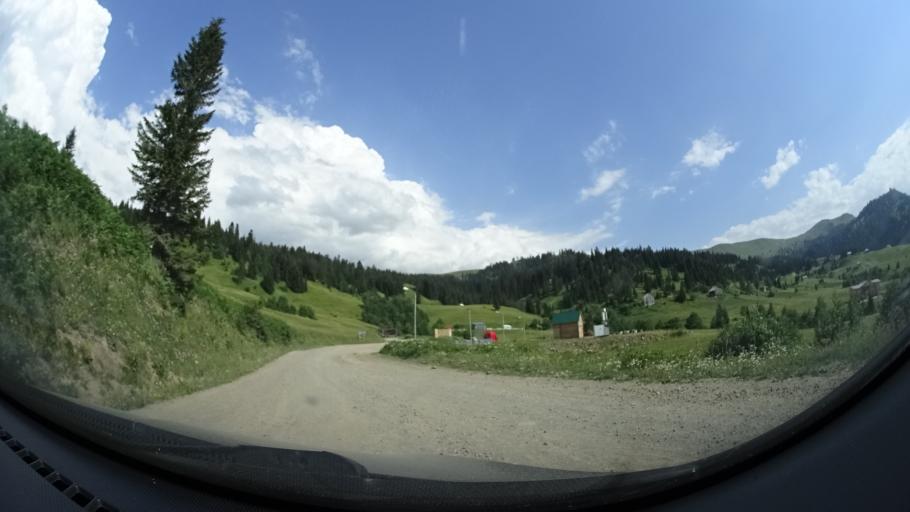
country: GE
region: Ajaria
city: Dioknisi
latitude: 41.6400
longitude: 42.4942
